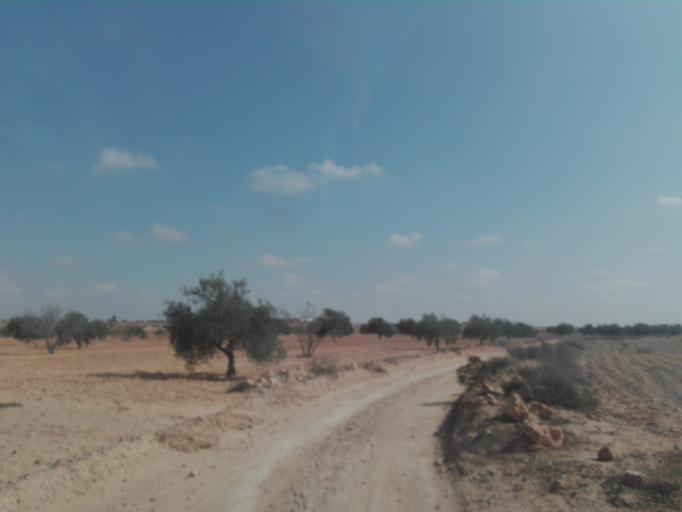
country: TN
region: Madanin
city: Medenine
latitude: 33.4360
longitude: 10.4247
